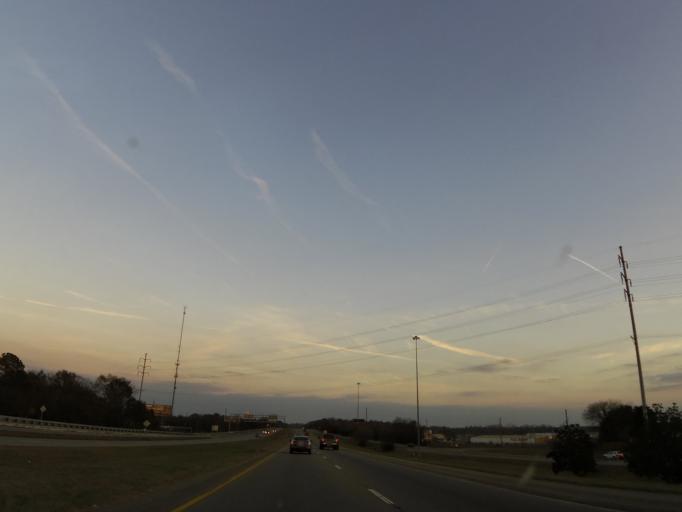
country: US
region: Georgia
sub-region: Dougherty County
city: Albany
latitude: 31.6060
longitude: -84.1540
